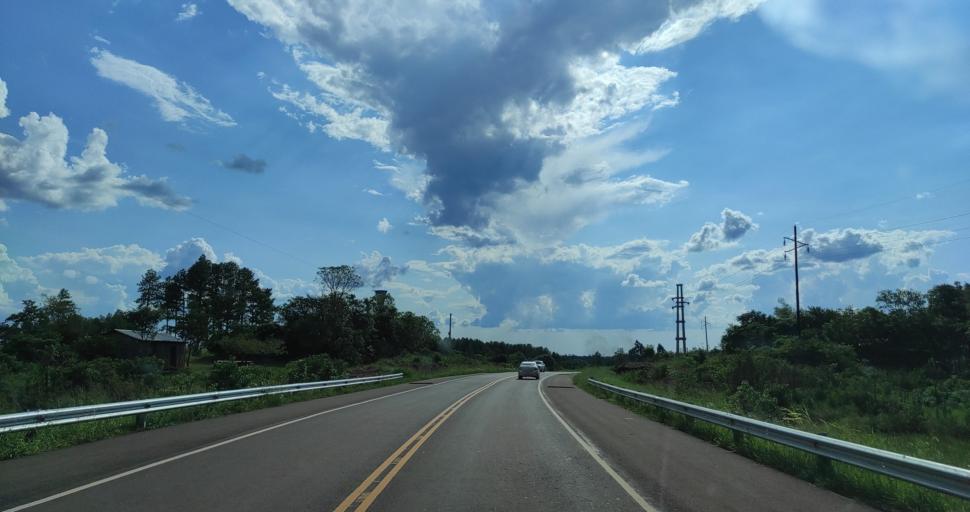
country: AR
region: Misiones
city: Bernardo de Irigoyen
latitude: -26.2992
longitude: -53.8014
